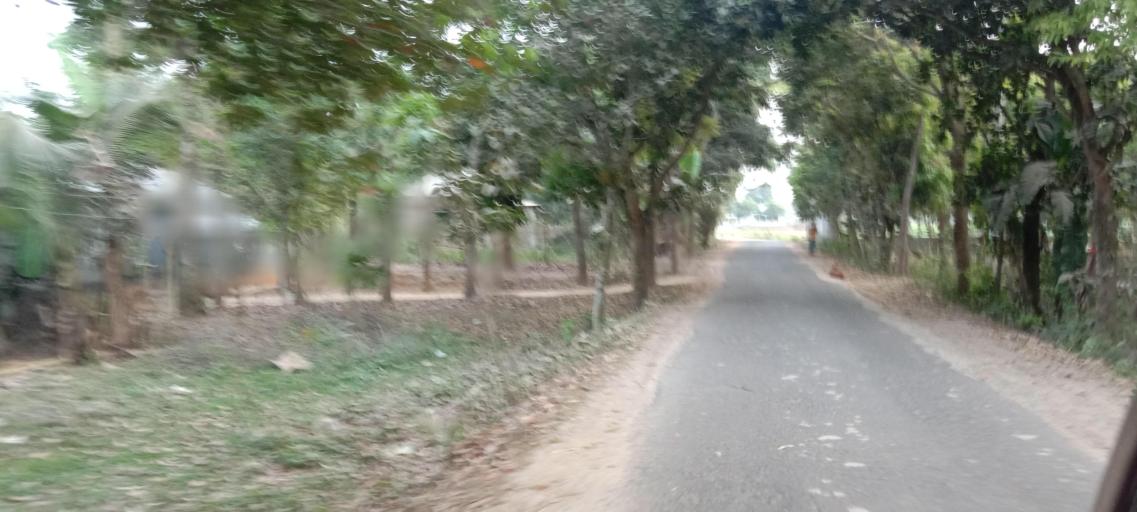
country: BD
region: Dhaka
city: Sakhipur
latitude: 24.4383
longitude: 90.2626
